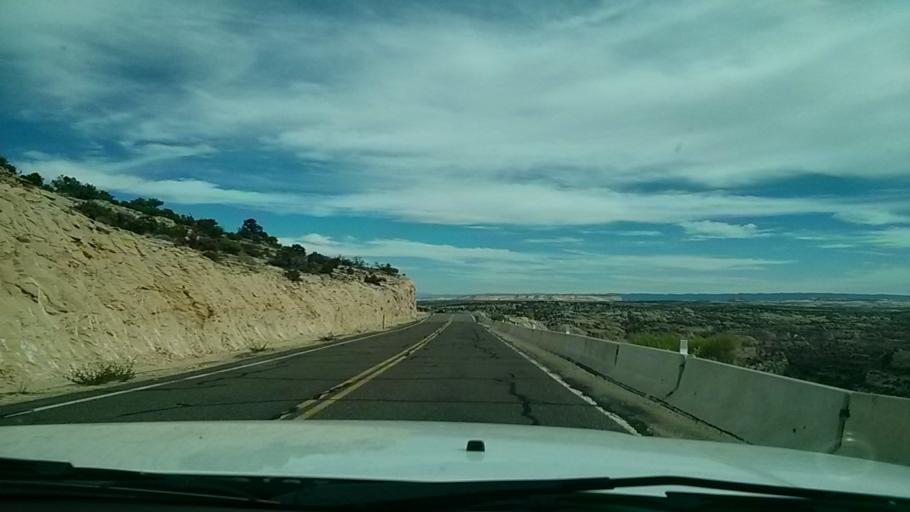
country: US
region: Utah
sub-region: Wayne County
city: Loa
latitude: 37.8202
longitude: -111.4124
